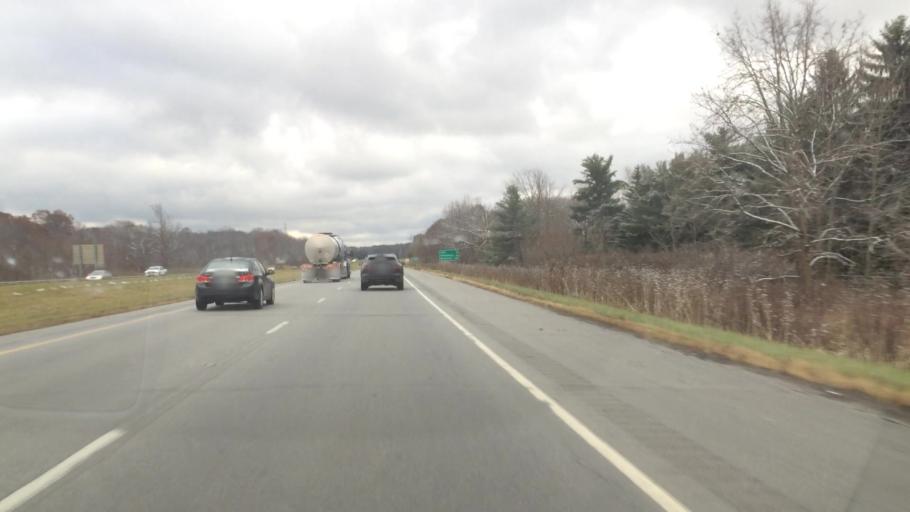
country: US
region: Ohio
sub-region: Summit County
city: Twinsburg
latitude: 41.2989
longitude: -81.4287
